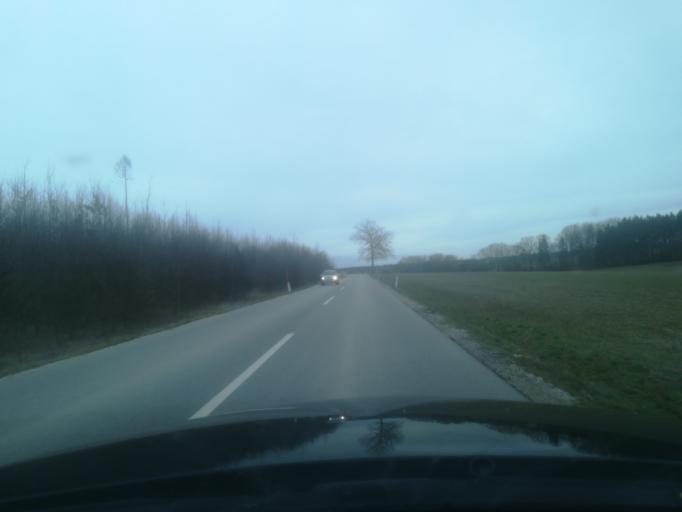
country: AT
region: Upper Austria
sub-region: Wels-Land
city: Bad Wimsbach-Neydharting
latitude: 48.0719
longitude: 13.9334
